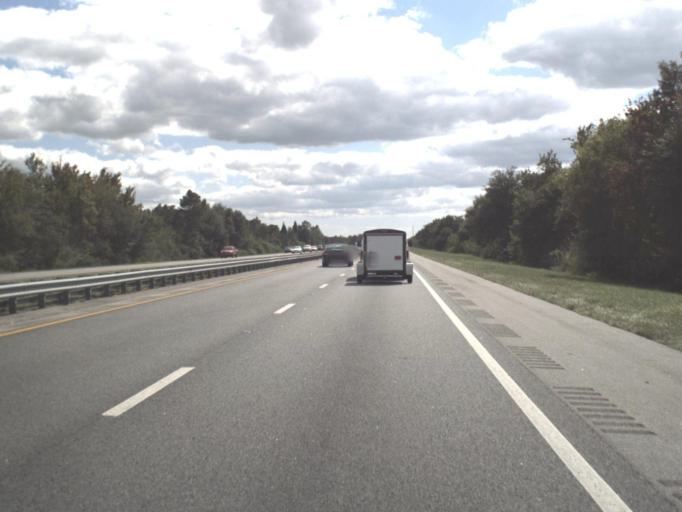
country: US
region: Florida
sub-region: Osceola County
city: Saint Cloud
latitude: 28.1657
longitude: -81.3012
